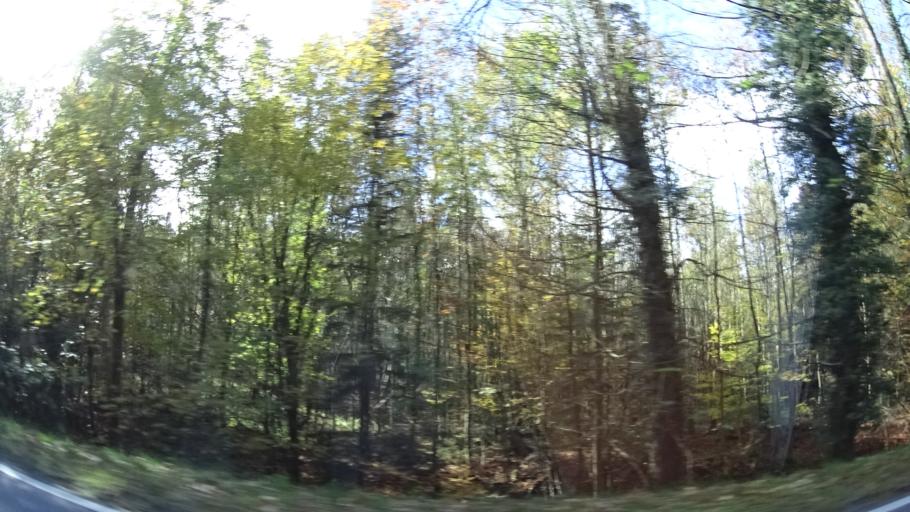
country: DE
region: Baden-Wuerttemberg
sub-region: Karlsruhe Region
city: Tiefenbronn
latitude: 48.8518
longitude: 8.7664
